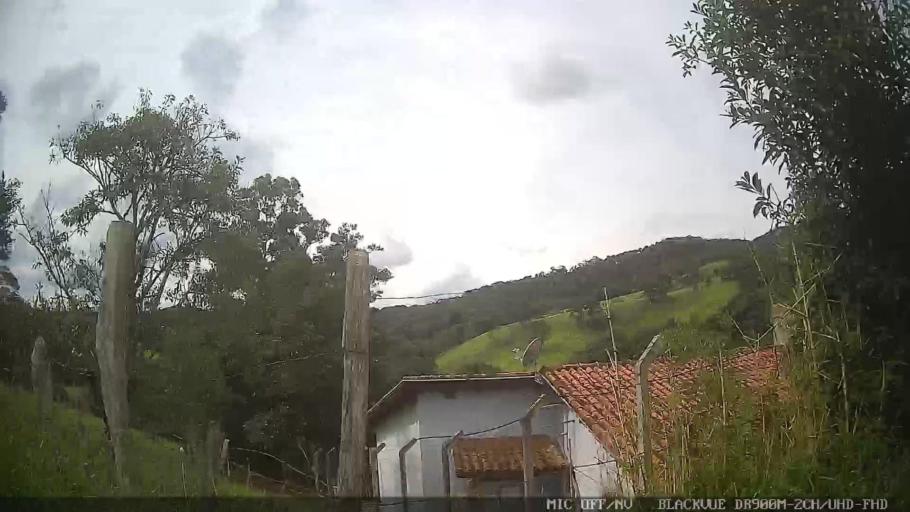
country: BR
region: Minas Gerais
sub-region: Extrema
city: Extrema
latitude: -22.8340
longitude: -46.2794
